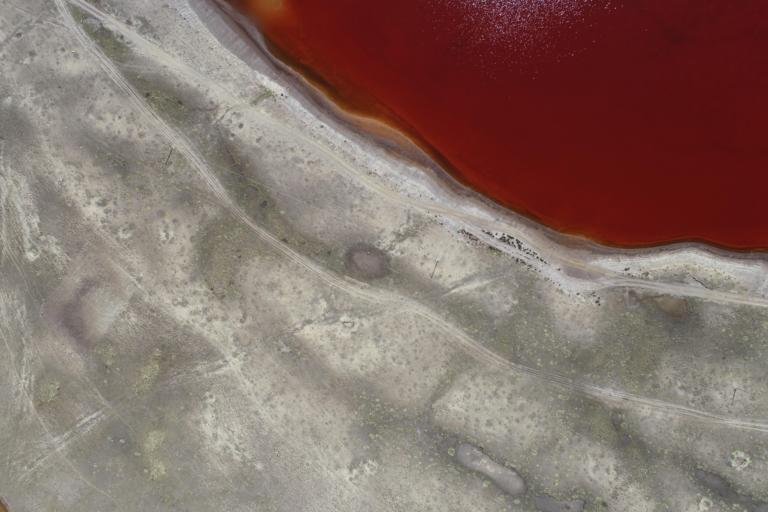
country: BO
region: La Paz
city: La Paz
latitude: -16.3437
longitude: -68.1618
